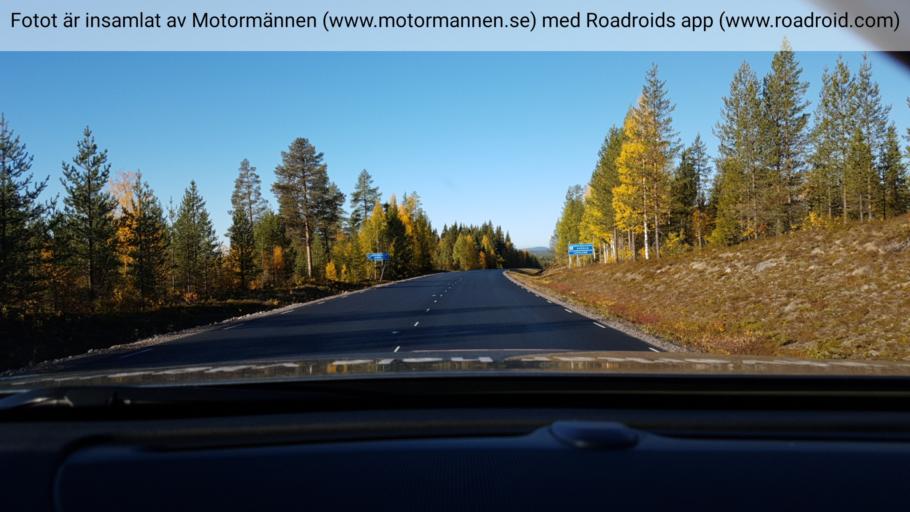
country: SE
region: Vaesterbotten
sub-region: Norsjo Kommun
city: Norsjoe
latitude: 65.4101
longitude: 19.7914
